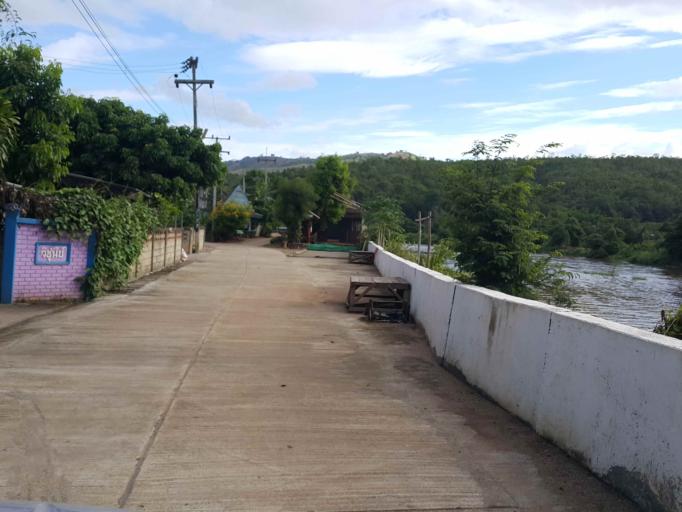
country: TH
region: Chiang Mai
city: Mae Chaem
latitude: 18.4967
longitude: 98.3620
